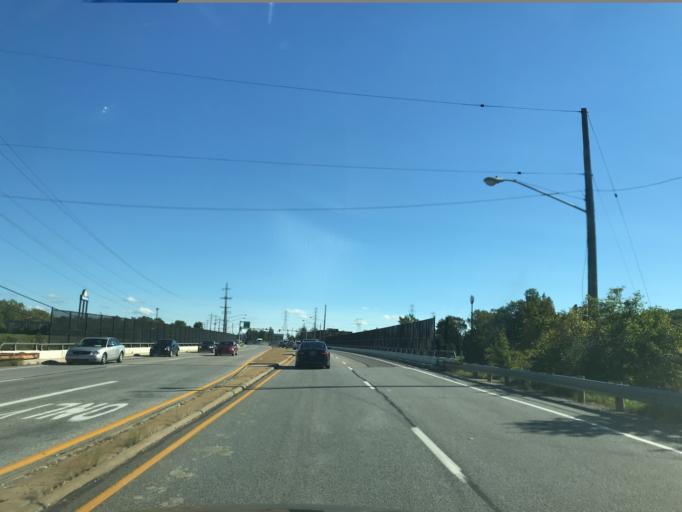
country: US
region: Ohio
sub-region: Lake County
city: Kirtland
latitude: 41.6414
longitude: -81.3745
